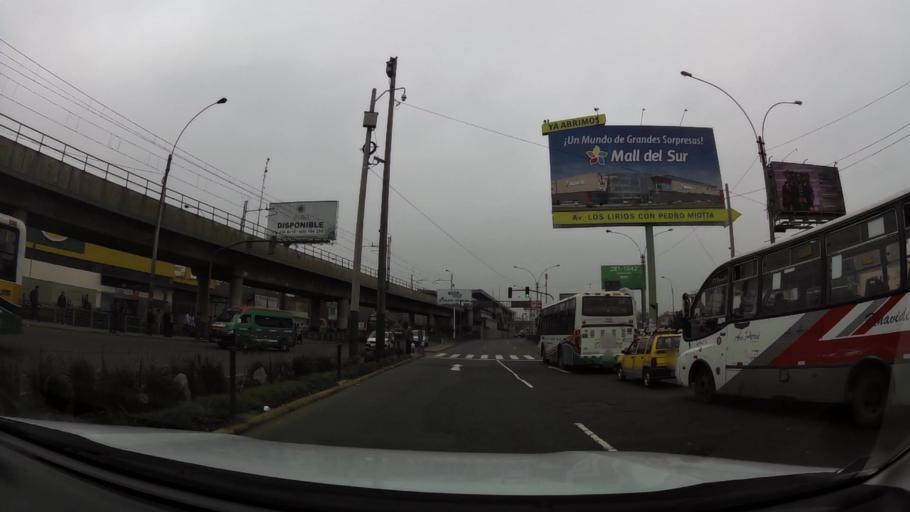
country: PE
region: Lima
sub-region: Lima
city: Surco
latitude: -12.1505
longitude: -76.9810
